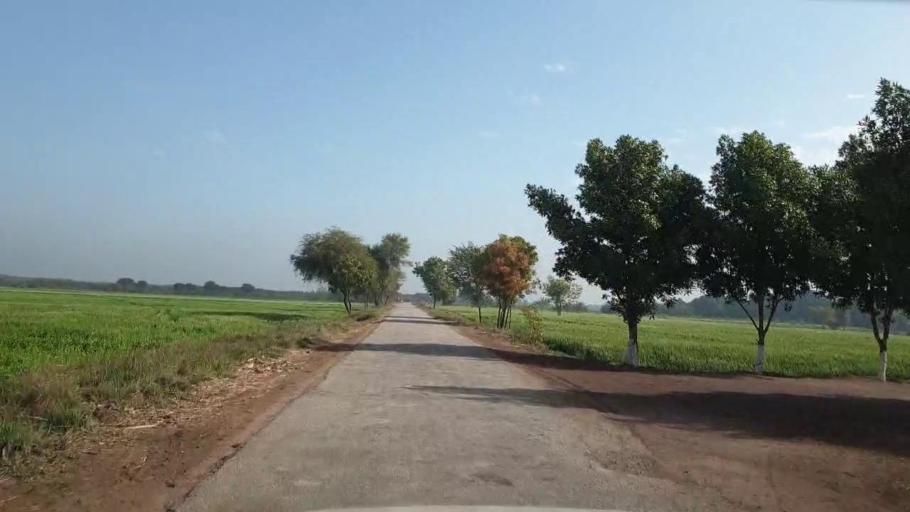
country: PK
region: Sindh
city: Matiari
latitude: 25.5958
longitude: 68.4878
